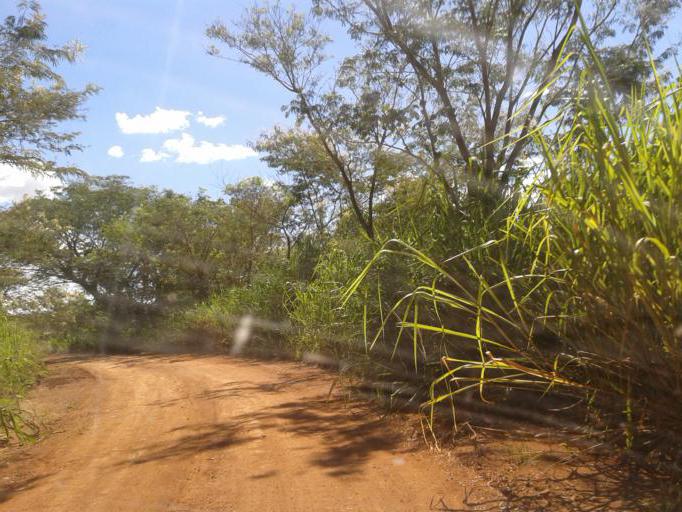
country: BR
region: Minas Gerais
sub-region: Capinopolis
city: Capinopolis
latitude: -18.5918
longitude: -49.6242
